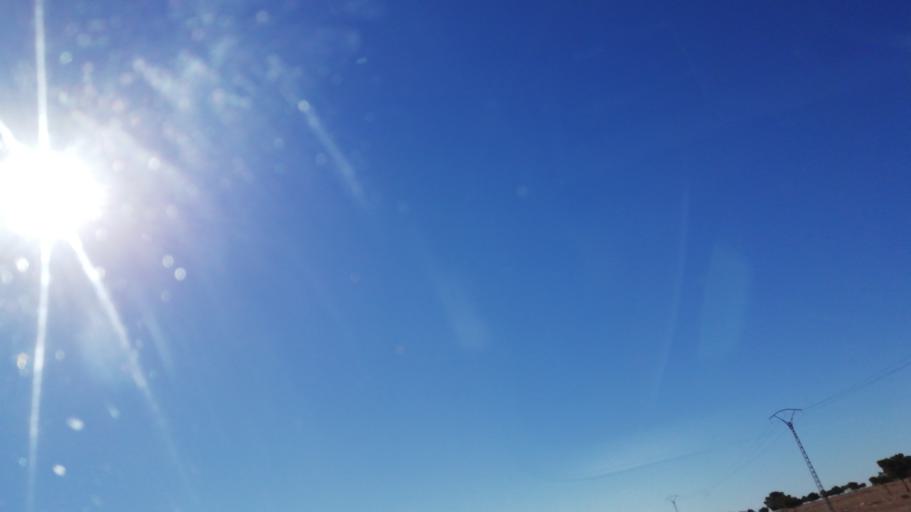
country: DZ
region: Saida
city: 'Ain el Hadjar
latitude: 34.0283
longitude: 0.0716
